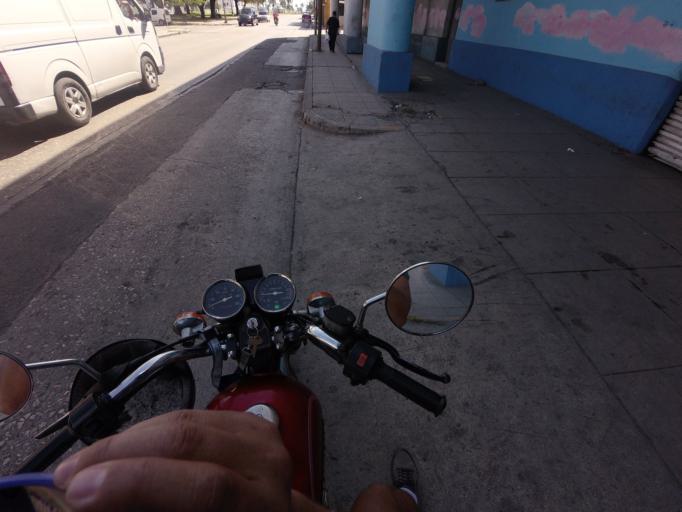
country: CU
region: La Habana
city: La Habana Vieja
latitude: 23.1132
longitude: -82.3590
